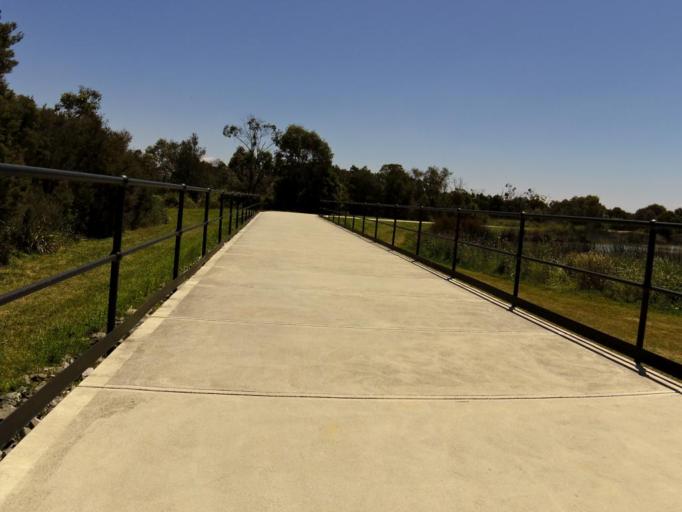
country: AU
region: Victoria
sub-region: Casey
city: Berwick
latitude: -38.0641
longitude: 145.3292
